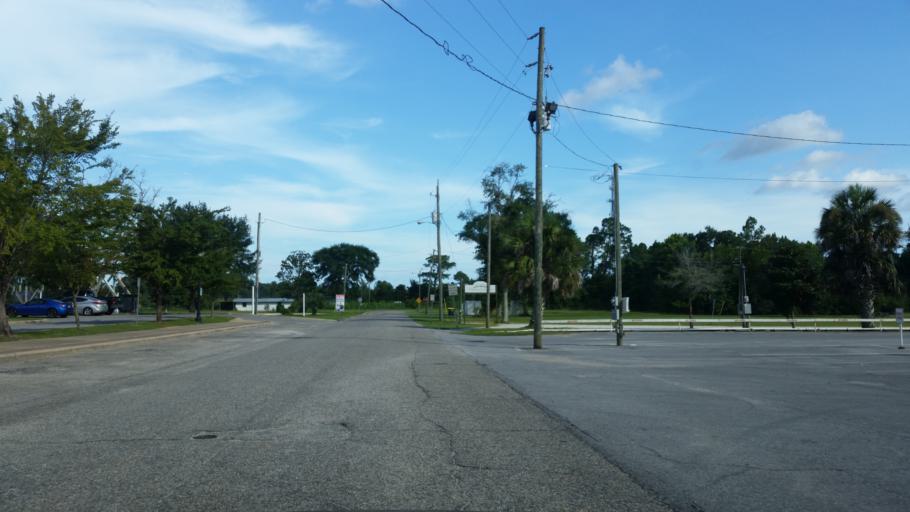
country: US
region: Florida
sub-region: Santa Rosa County
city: Milton
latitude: 30.6225
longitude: -87.0355
